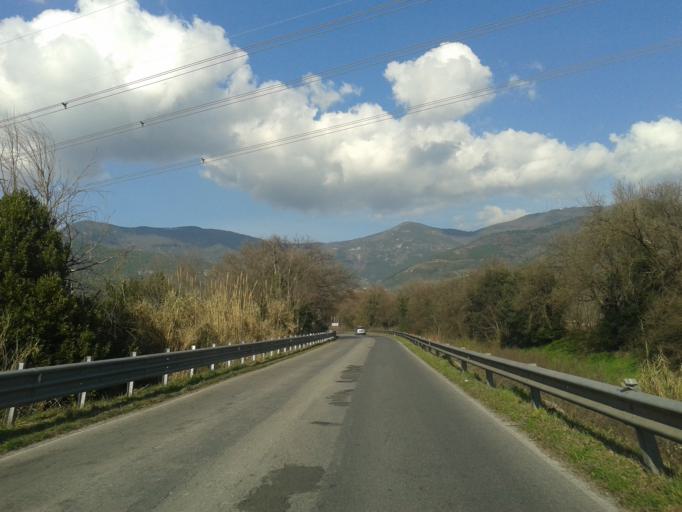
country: IT
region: Tuscany
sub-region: Province of Pisa
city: Calci
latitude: 43.7148
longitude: 10.5092
